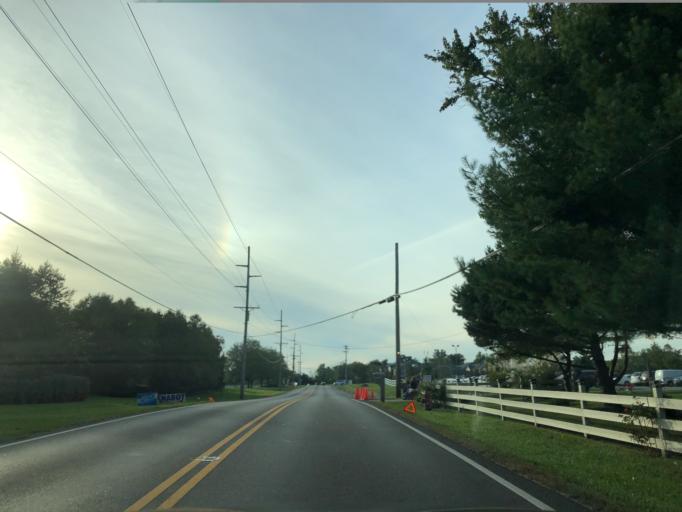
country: US
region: Ohio
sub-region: Warren County
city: Landen
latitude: 39.2903
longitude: -84.2857
